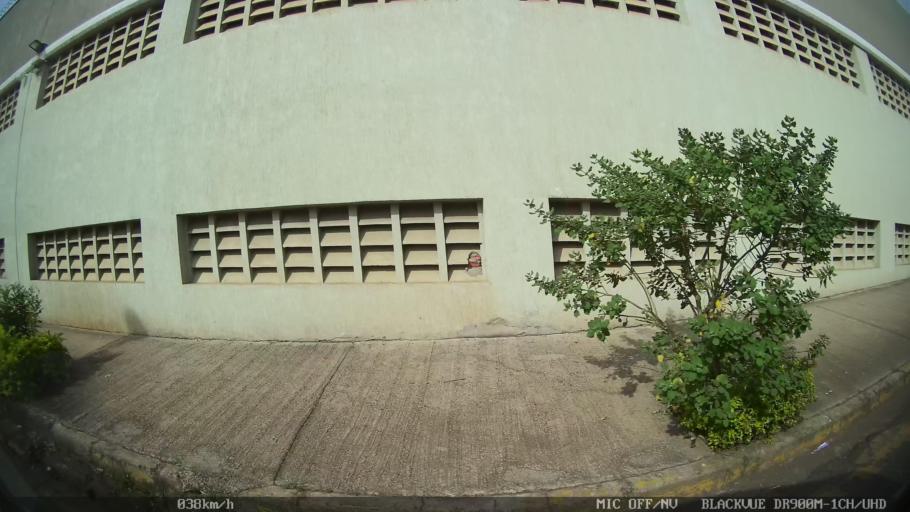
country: BR
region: Sao Paulo
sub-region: Piracicaba
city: Piracicaba
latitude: -22.7362
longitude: -47.6507
